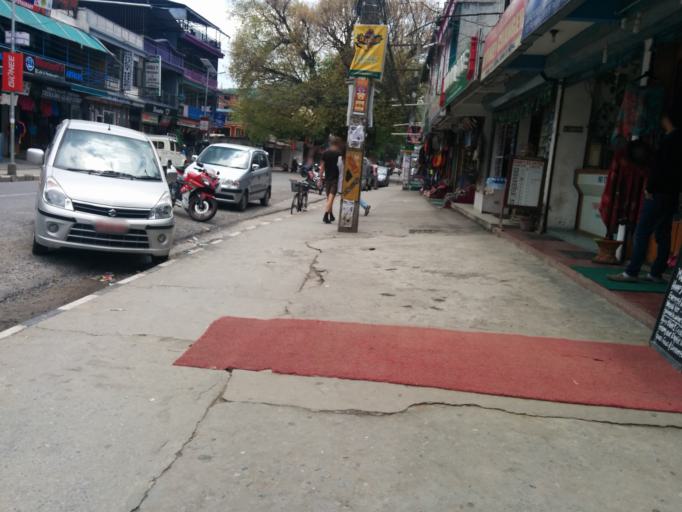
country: NP
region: Western Region
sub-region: Gandaki Zone
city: Pokhara
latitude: 28.2114
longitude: 83.9571
